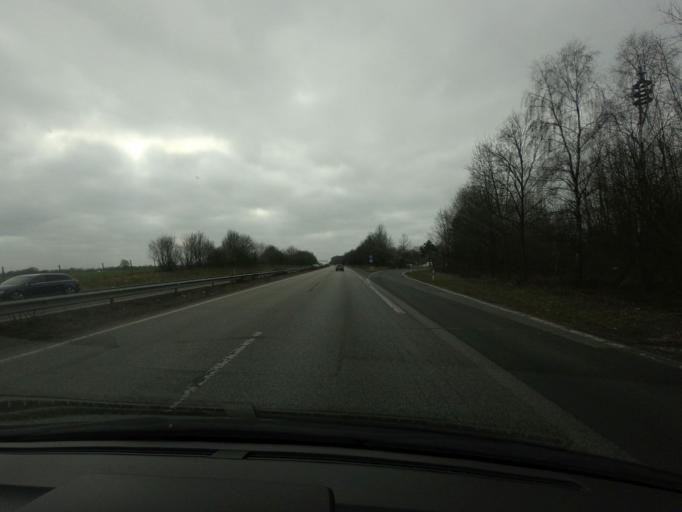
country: DE
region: Lower Saxony
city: Buchholz in der Nordheide
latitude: 53.3917
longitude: 9.8837
